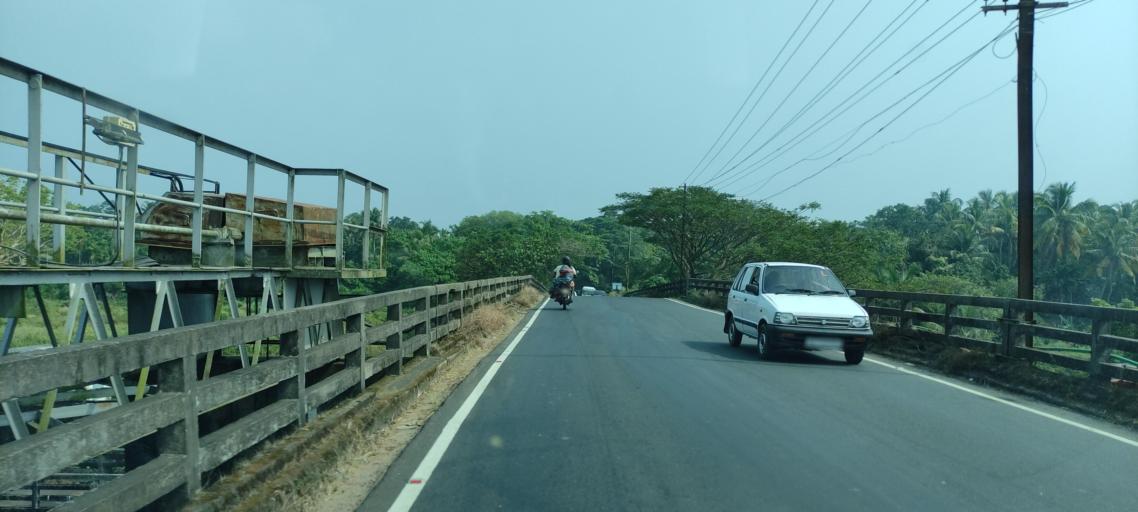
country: IN
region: Kerala
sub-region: Alappuzha
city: Shertallai
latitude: 9.6724
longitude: 76.4054
